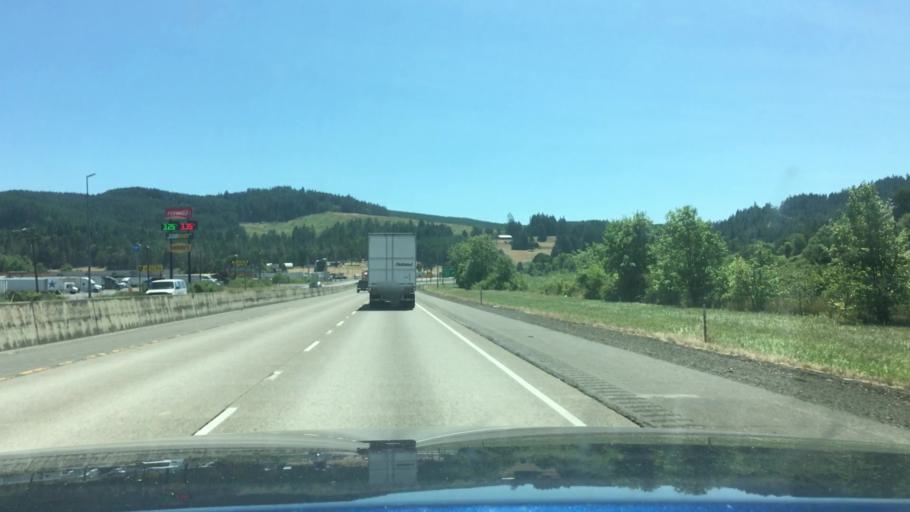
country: US
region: Oregon
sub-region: Douglas County
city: Yoncalla
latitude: 43.5418
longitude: -123.2901
